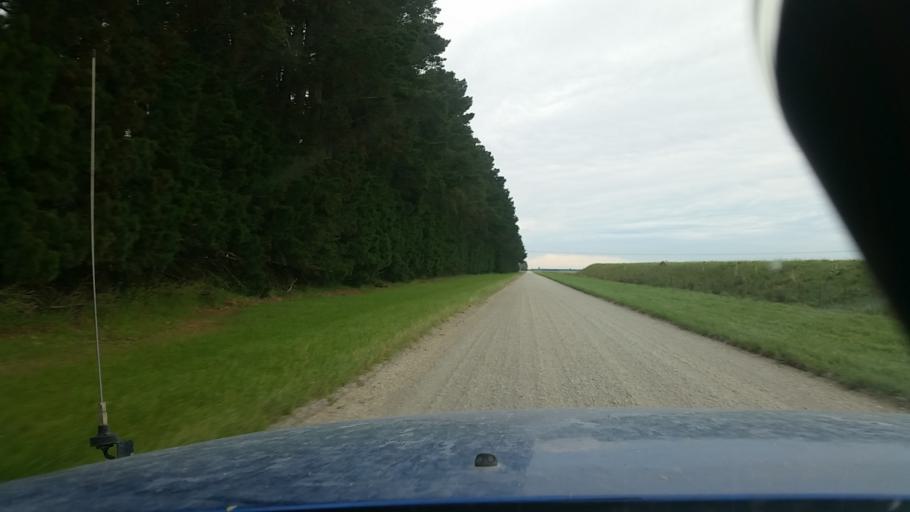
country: NZ
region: Canterbury
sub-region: Ashburton District
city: Tinwald
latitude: -43.8854
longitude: 171.5179
